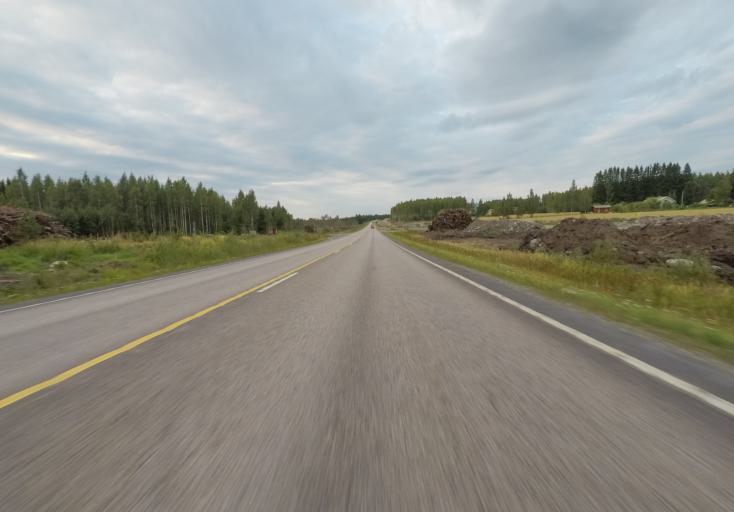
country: FI
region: Central Finland
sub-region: Joutsa
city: Leivonmaeki
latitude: 61.8589
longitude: 26.1028
